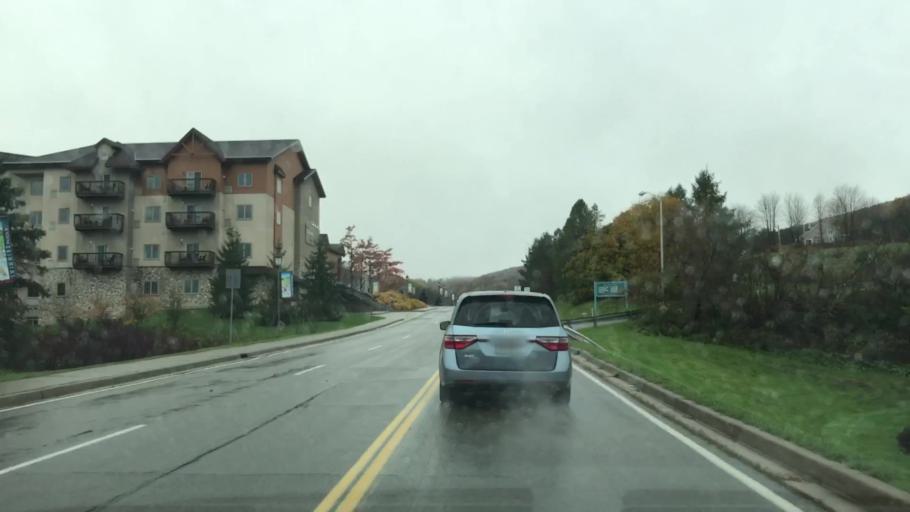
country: US
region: New York
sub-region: Cattaraugus County
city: Salamanca
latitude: 42.2630
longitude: -78.6650
